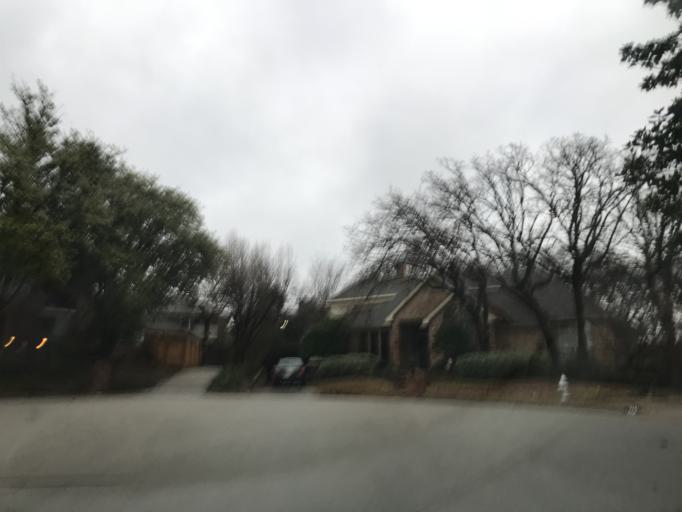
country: US
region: Texas
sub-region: Tarrant County
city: Arlington
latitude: 32.7723
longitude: -97.1029
